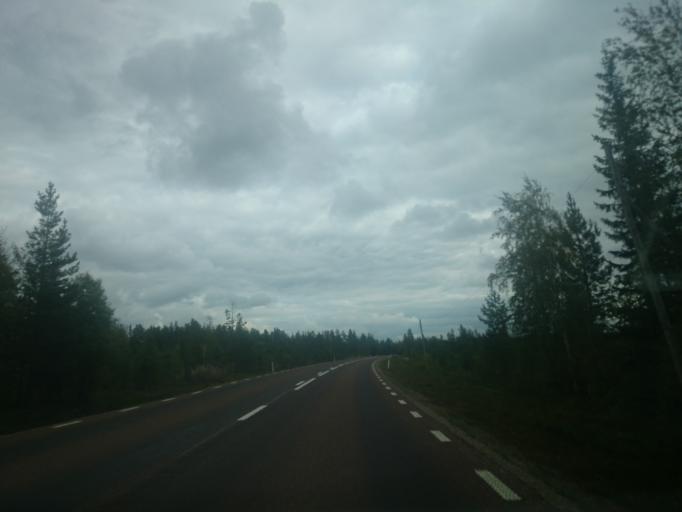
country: SE
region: Jaemtland
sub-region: Harjedalens Kommun
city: Sveg
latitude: 62.0549
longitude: 14.5454
